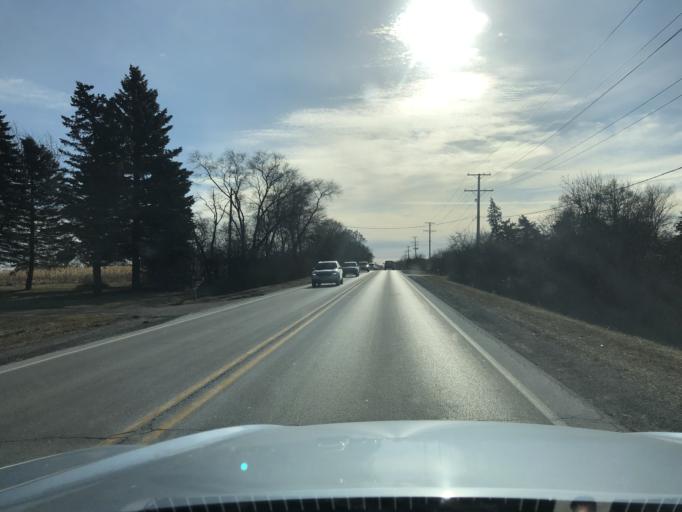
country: US
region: Illinois
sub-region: Lake County
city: Grandwood Park
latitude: 42.3906
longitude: -88.0041
